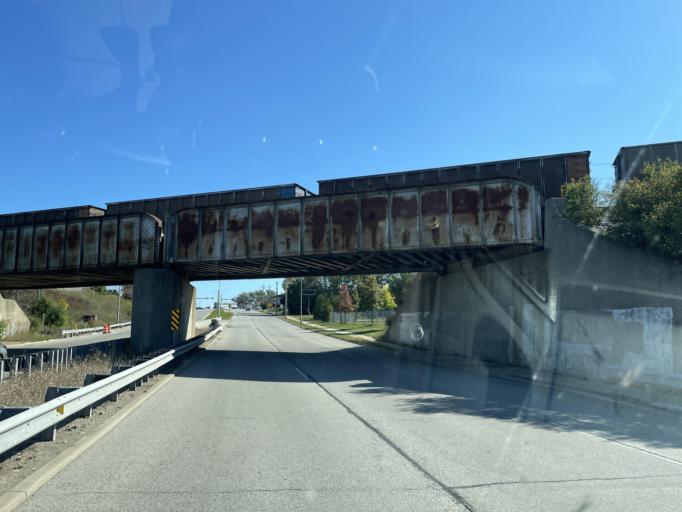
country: US
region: Wisconsin
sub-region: Waukesha County
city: Butler
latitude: 43.1238
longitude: -88.0411
